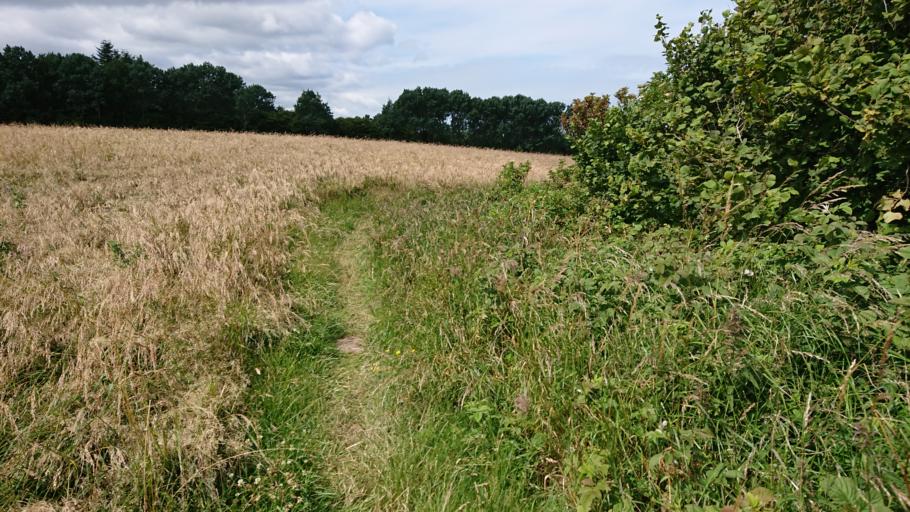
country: DK
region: North Denmark
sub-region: Jammerbugt Kommune
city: Brovst
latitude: 57.1316
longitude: 9.4047
